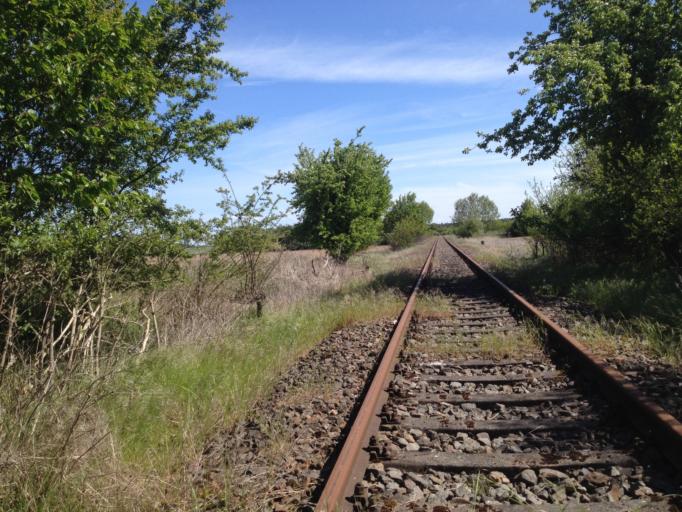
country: DE
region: Brandenburg
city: Templin
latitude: 53.1203
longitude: 13.4521
